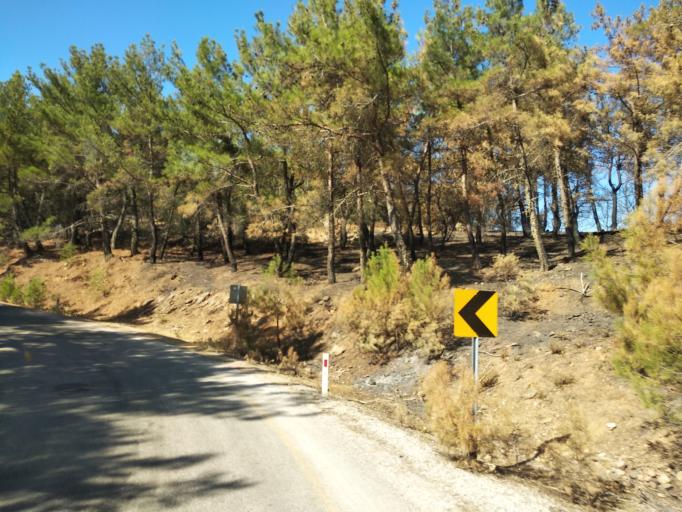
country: TR
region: Izmir
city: Gaziemir
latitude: 38.3081
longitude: 26.9988
